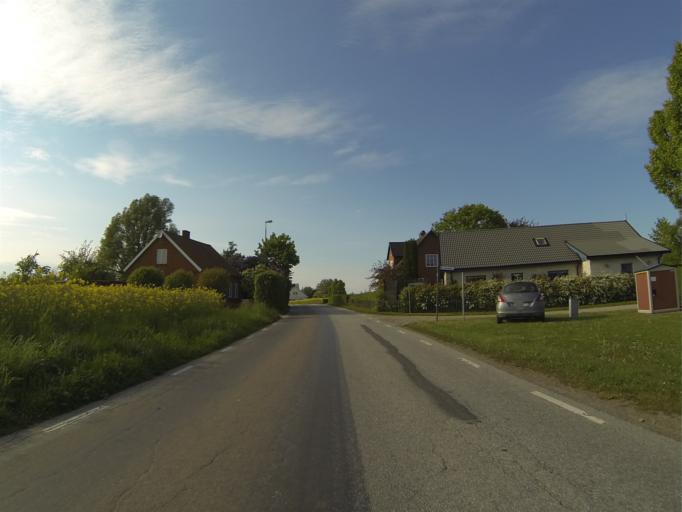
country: SE
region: Skane
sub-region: Svedala Kommun
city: Klagerup
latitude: 55.6484
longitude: 13.2663
